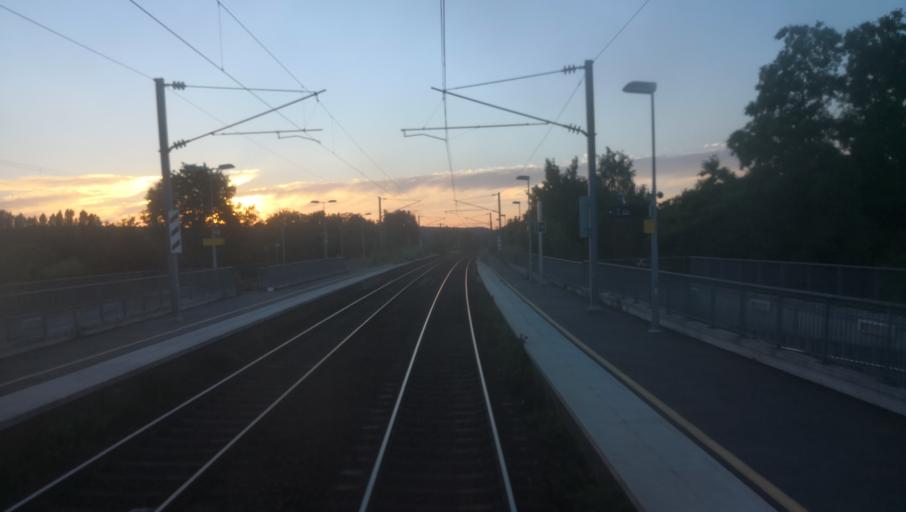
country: FR
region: Haute-Normandie
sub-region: Departement de l'Eure
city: Bueil
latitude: 48.9256
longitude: 1.4430
